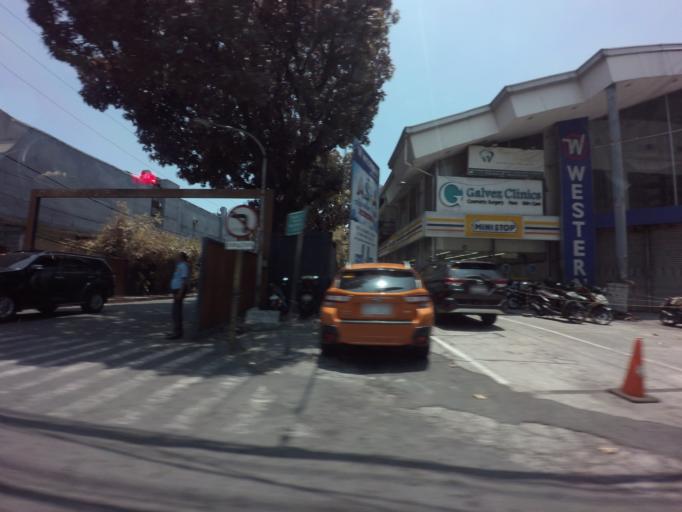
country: PH
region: Metro Manila
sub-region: Makati City
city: Makati City
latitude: 14.5484
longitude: 121.0252
